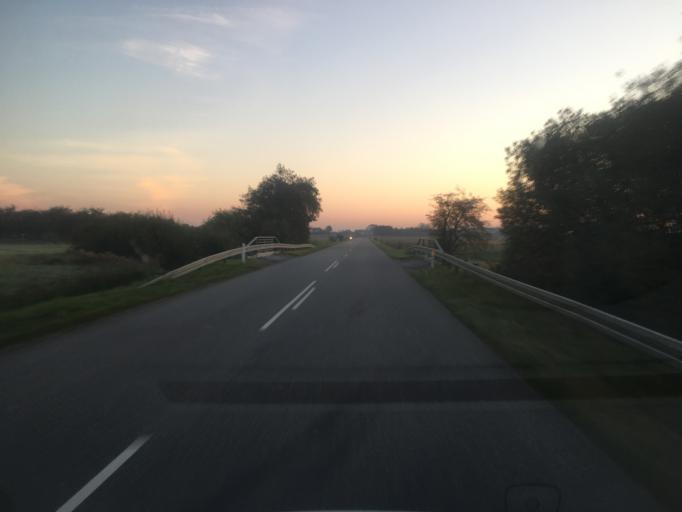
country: DK
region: South Denmark
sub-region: Aabenraa Kommune
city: Tinglev
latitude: 54.9714
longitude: 9.1264
